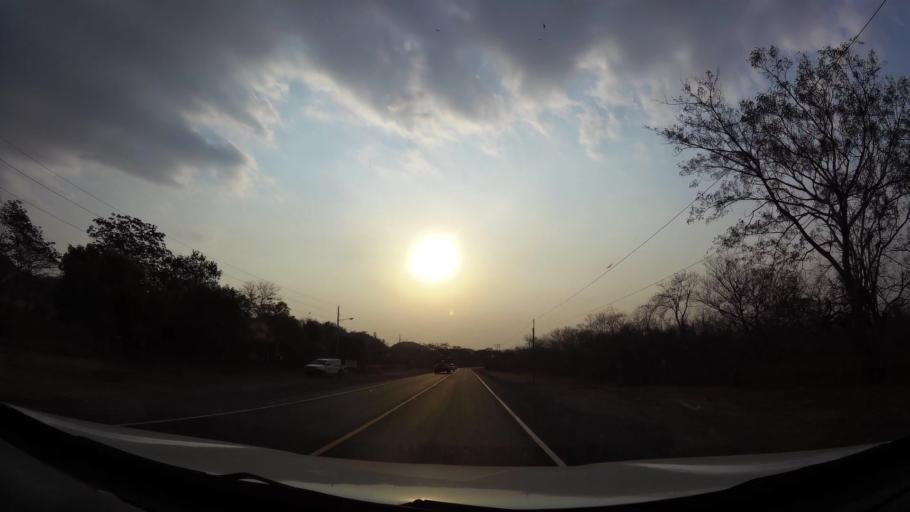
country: NI
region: Leon
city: Nagarote
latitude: 12.2789
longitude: -86.5068
